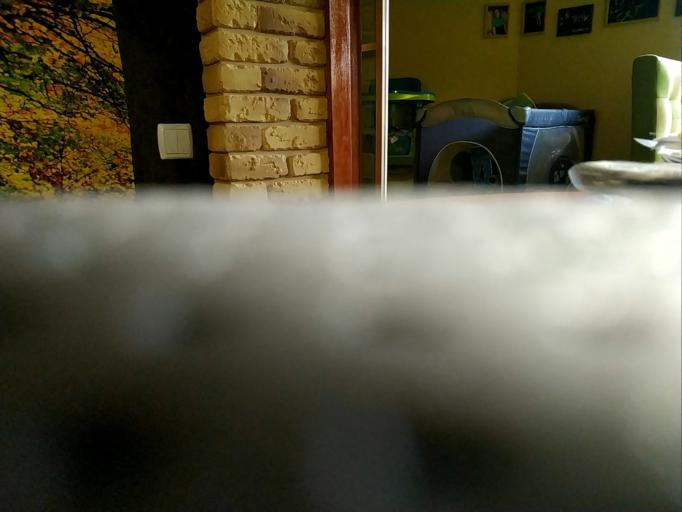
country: RU
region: Kaluga
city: Seredeyskiy
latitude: 53.8694
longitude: 35.3671
